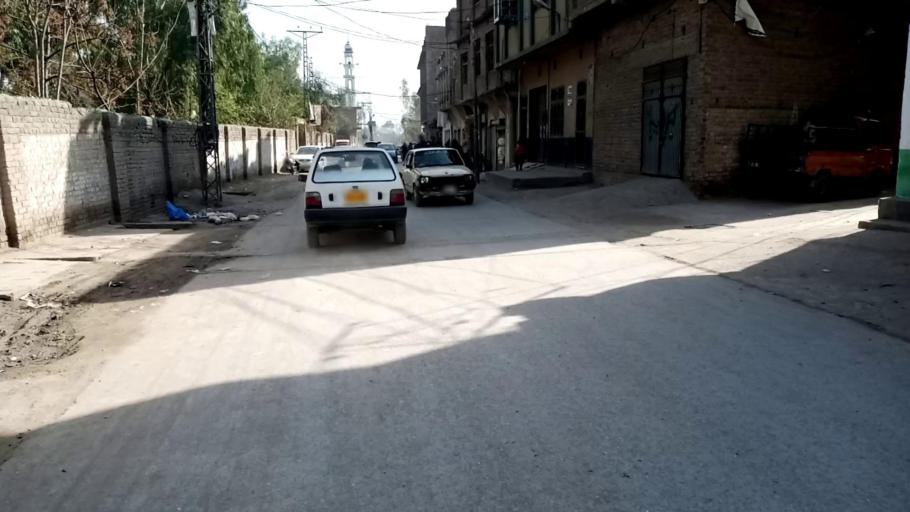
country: PK
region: Khyber Pakhtunkhwa
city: Peshawar
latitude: 33.9964
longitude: 71.5828
